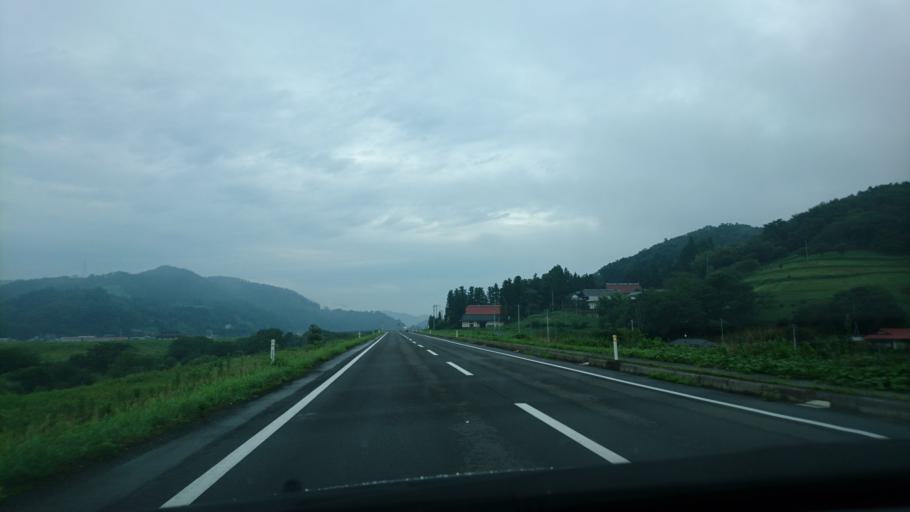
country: JP
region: Iwate
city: Ichinoseki
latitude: 38.9108
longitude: 141.2581
